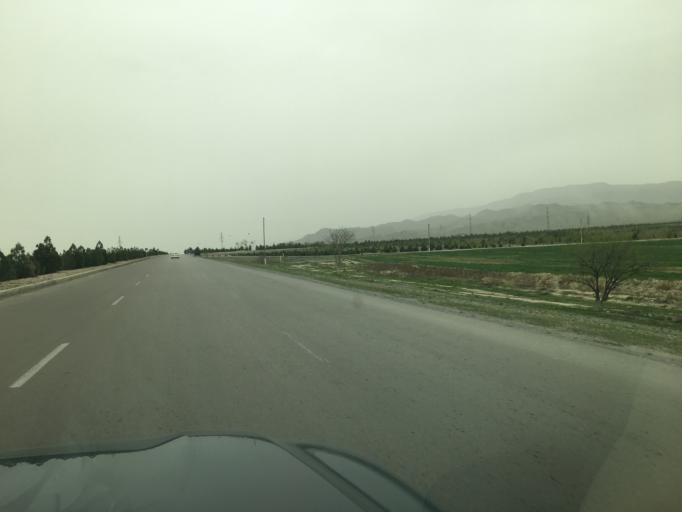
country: TM
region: Ahal
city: Baharly
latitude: 38.2858
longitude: 57.6588
